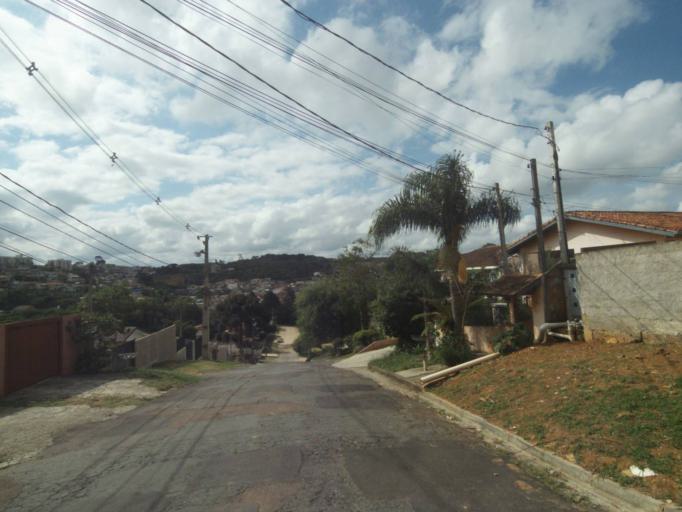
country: BR
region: Parana
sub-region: Curitiba
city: Curitiba
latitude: -25.3800
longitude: -49.2972
